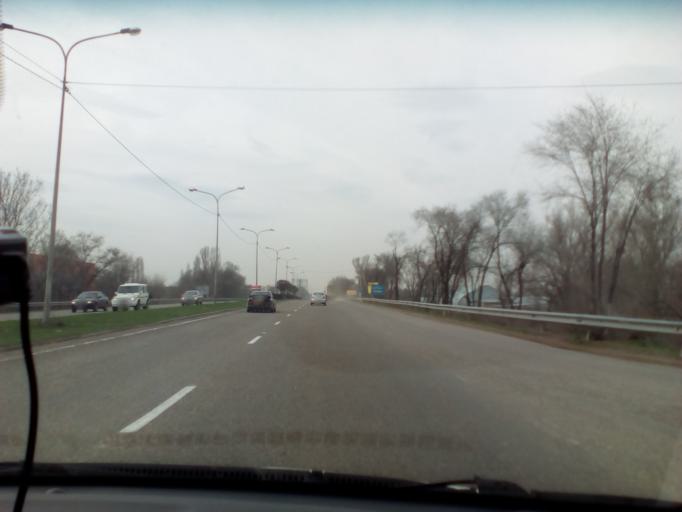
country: KZ
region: Almaty Oblysy
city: Burunday
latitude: 43.2186
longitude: 76.6454
